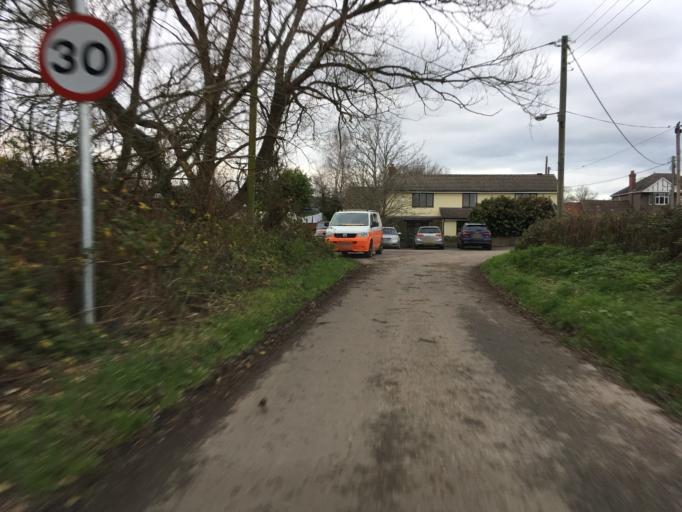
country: GB
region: Wales
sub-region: Monmouthshire
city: Magor
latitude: 51.5776
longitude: -2.8508
